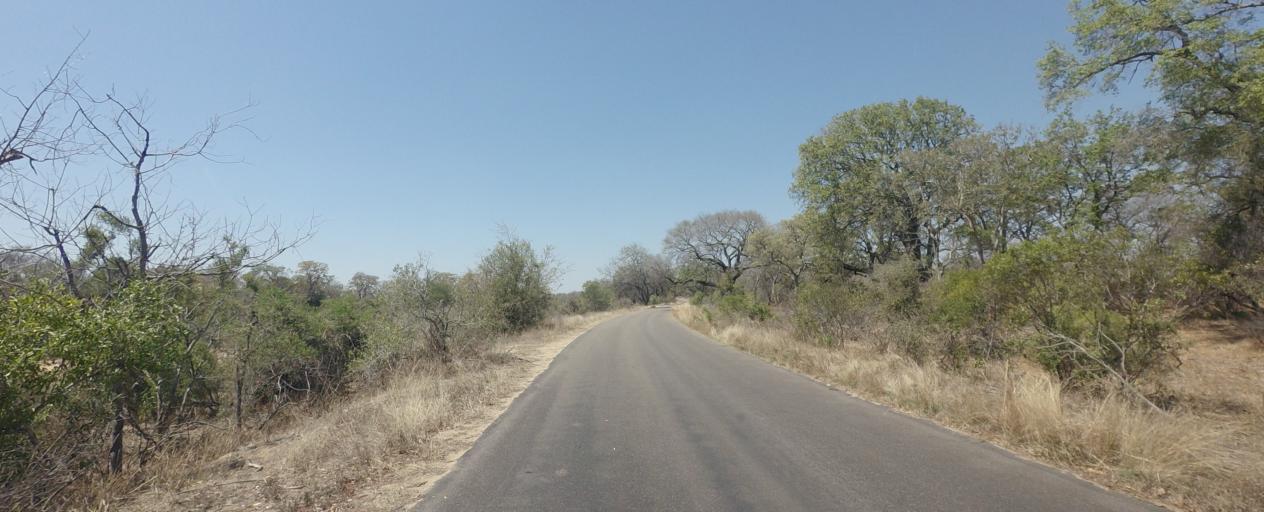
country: ZA
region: Limpopo
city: Thulamahashi
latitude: -24.4158
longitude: 31.5168
